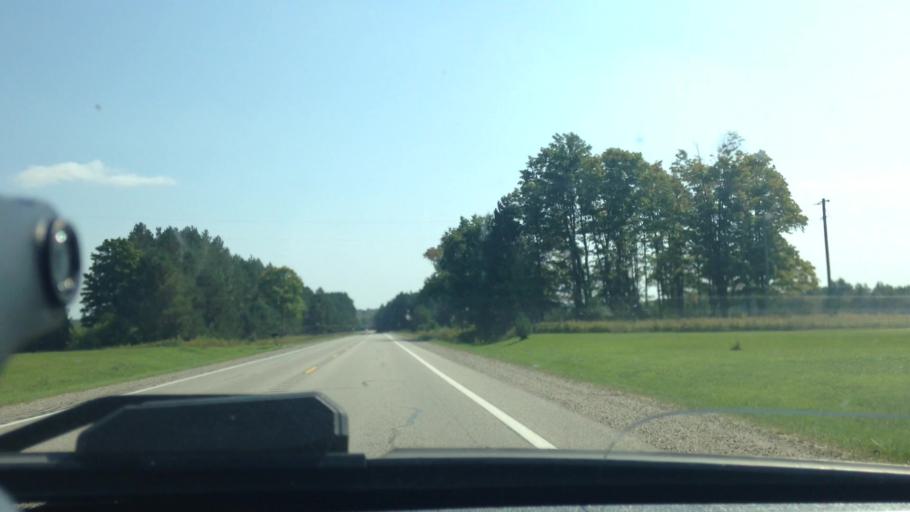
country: US
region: Michigan
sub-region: Luce County
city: Newberry
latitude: 46.3179
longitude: -85.6653
